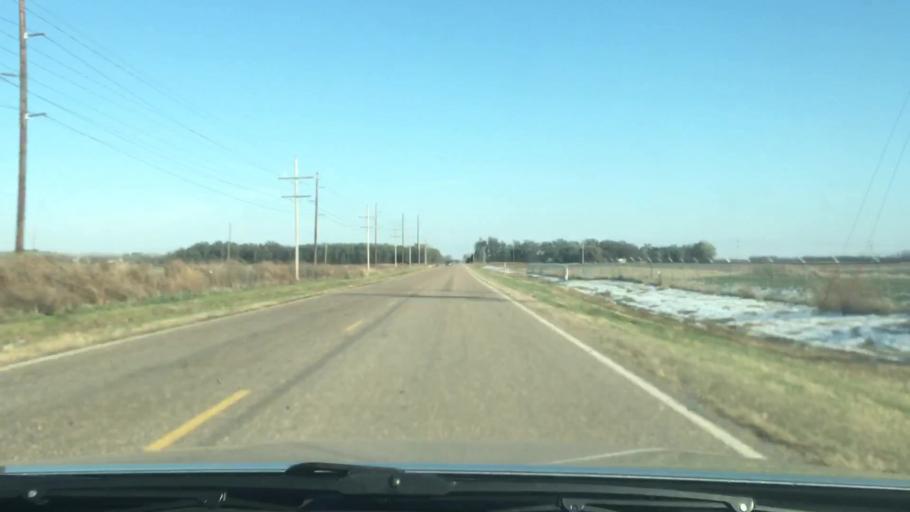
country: US
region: Kansas
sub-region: Rice County
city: Lyons
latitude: 38.2895
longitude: -98.1888
